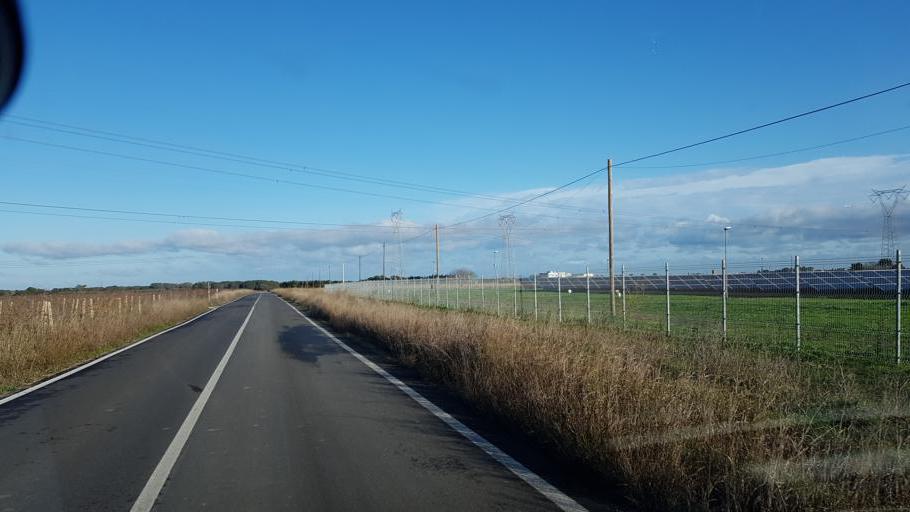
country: IT
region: Apulia
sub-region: Provincia di Brindisi
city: Tuturano
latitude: 40.5560
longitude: 17.9474
